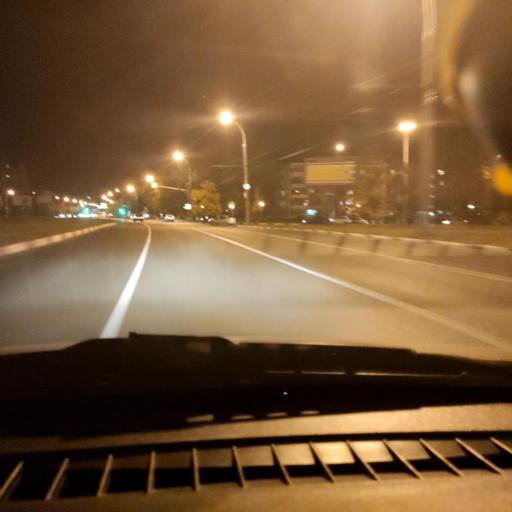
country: RU
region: Samara
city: Tol'yatti
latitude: 53.5189
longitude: 49.2942
